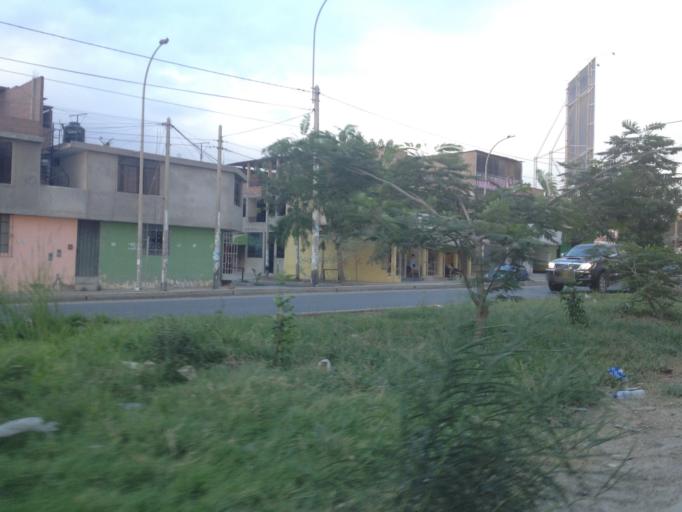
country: PE
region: Piura
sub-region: Provincia de Piura
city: Piura
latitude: -5.1821
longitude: -80.6410
